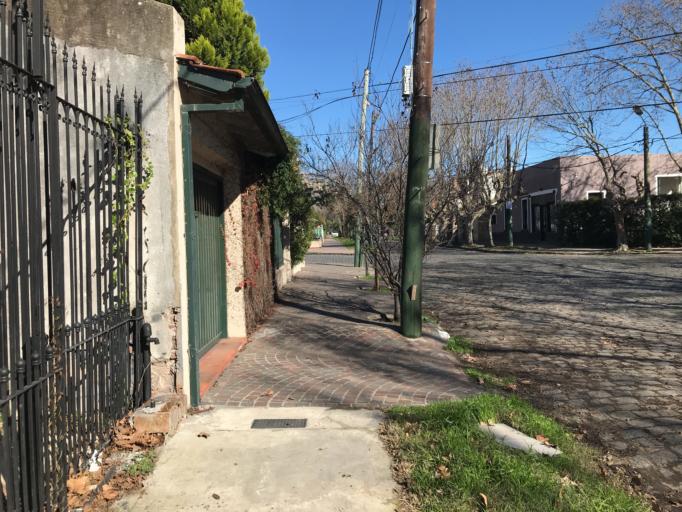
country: AR
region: Buenos Aires
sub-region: Partido de Lomas de Zamora
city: Lomas de Zamora
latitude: -34.7698
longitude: -58.3999
